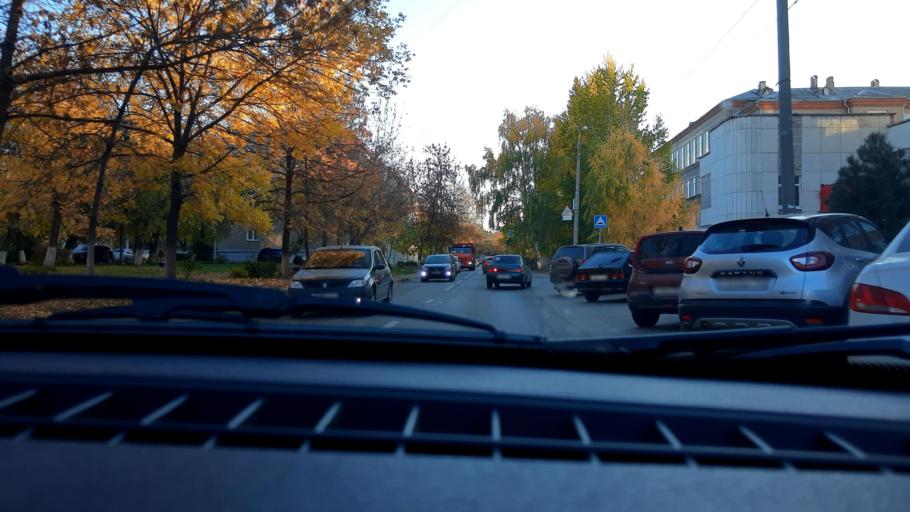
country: RU
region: Bashkortostan
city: Ufa
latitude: 54.7891
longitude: 56.0302
